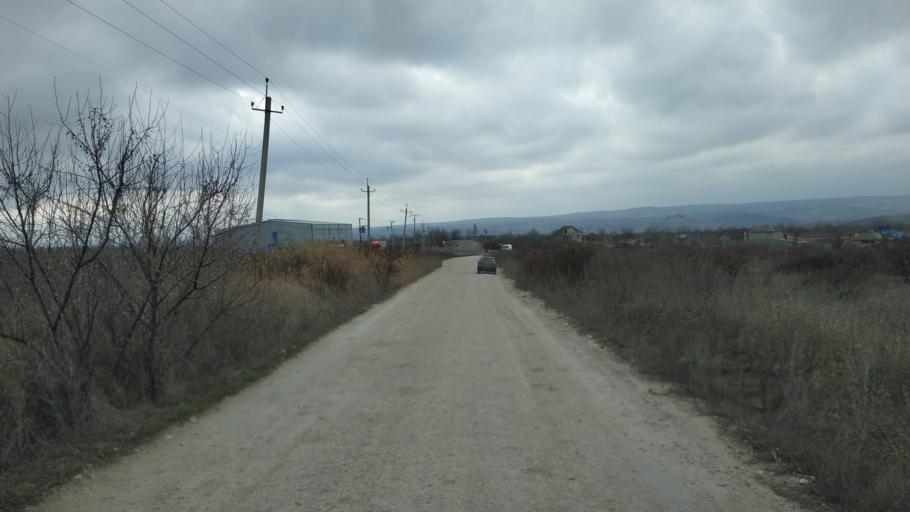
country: MD
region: Laloveni
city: Ialoveni
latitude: 46.9059
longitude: 28.7786
